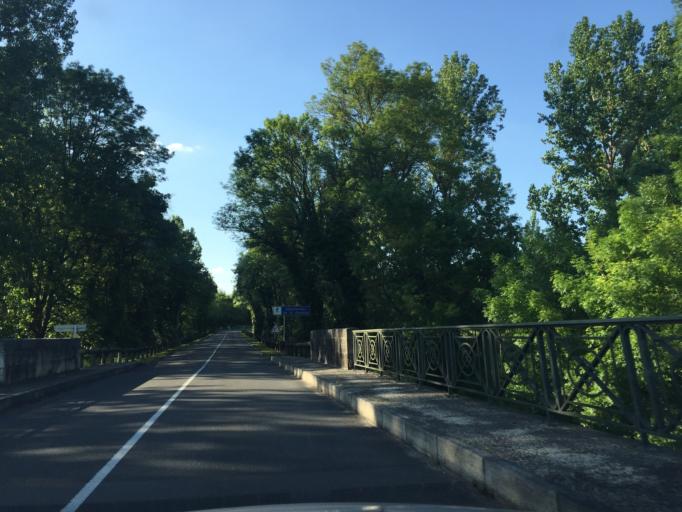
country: FR
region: Aquitaine
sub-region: Departement de la Dordogne
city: La Roche-Chalais
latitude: 45.2081
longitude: 0.0331
